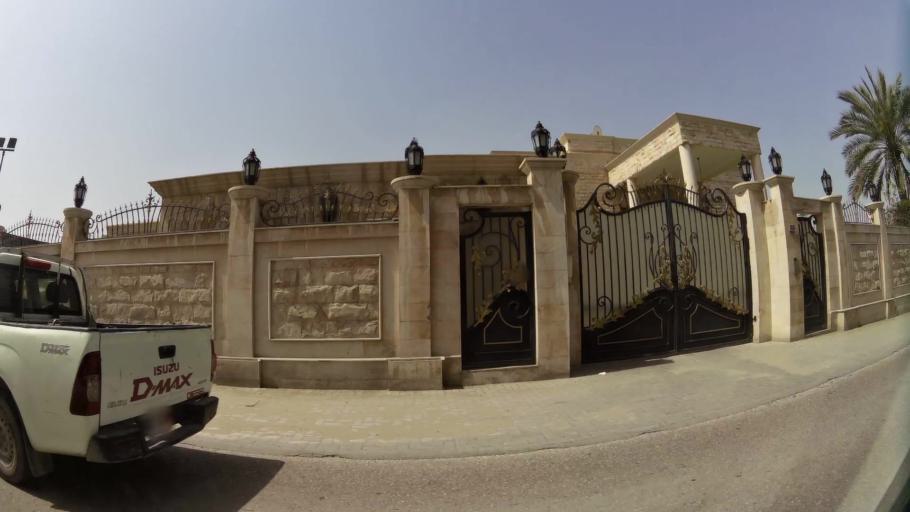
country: BH
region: Manama
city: Jidd Hafs
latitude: 26.2232
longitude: 50.4778
